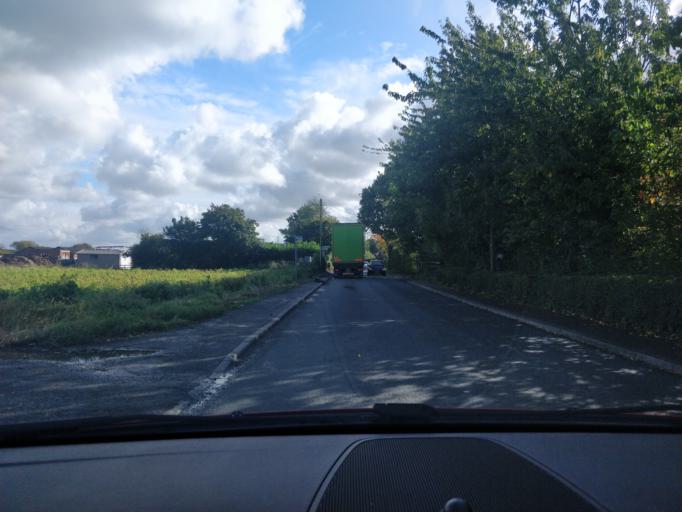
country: GB
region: England
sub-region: Lancashire
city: Ormskirk
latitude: 53.5984
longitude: -2.9001
